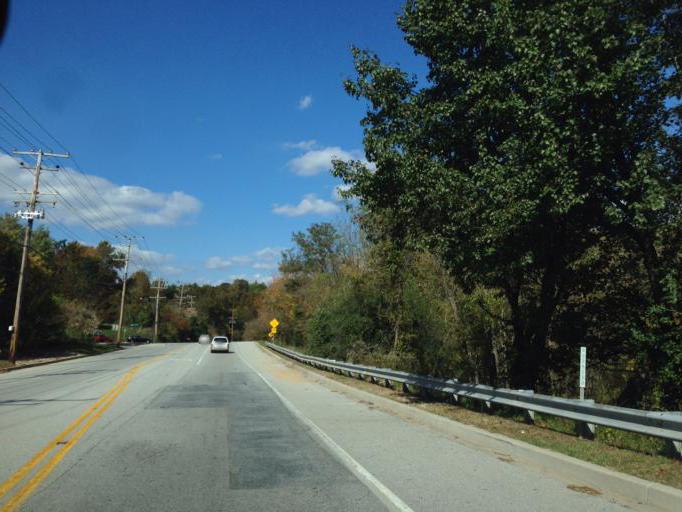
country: US
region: Maryland
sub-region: Baltimore County
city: Hunt Valley
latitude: 39.4995
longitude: -76.6505
